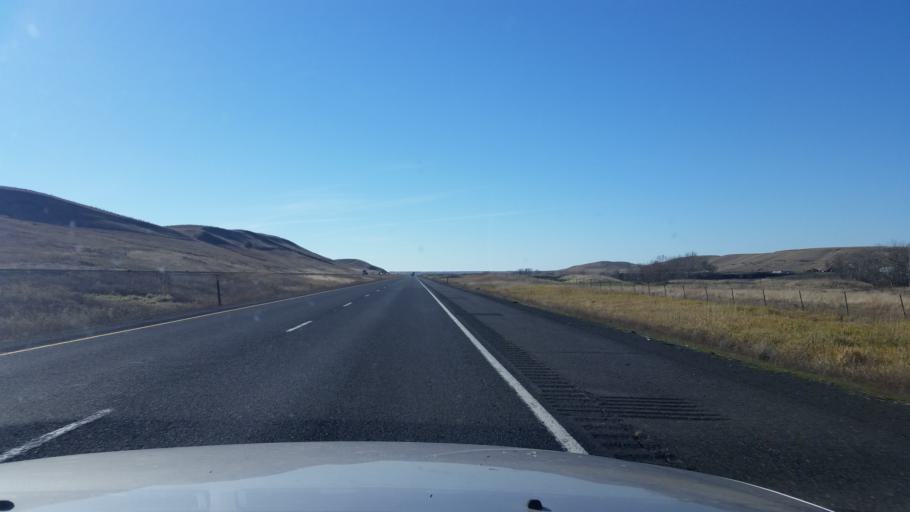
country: US
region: Washington
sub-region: Spokane County
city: Medical Lake
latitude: 47.3602
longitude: -117.8896
